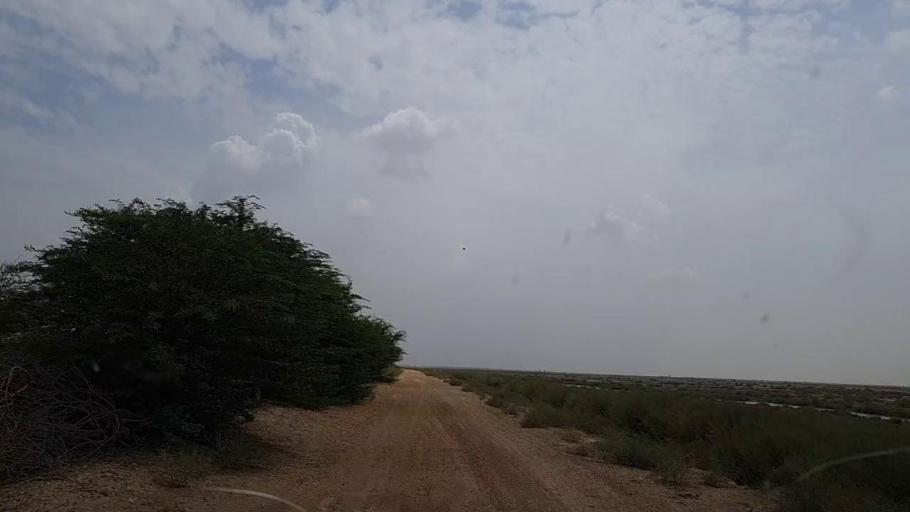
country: PK
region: Sindh
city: Phulji
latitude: 26.8040
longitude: 67.6039
